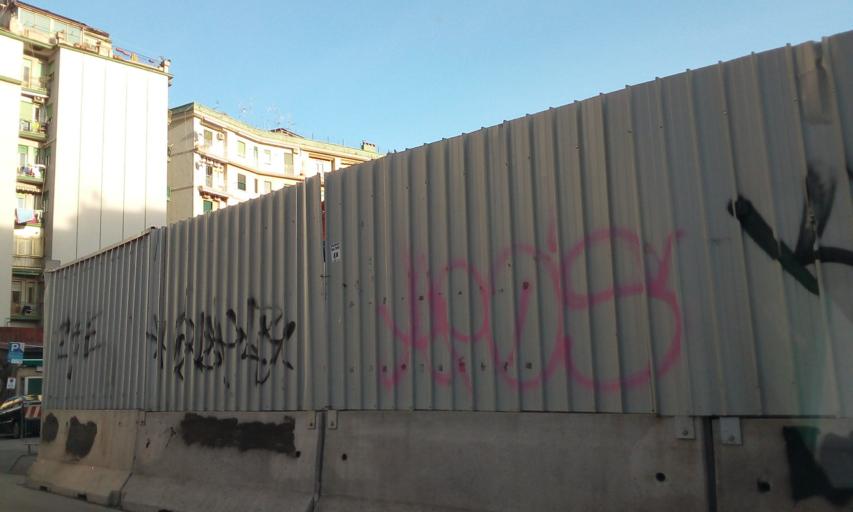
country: IT
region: Campania
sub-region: Provincia di Salerno
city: Capezzano Inferiore
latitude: 40.6788
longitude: 14.7680
